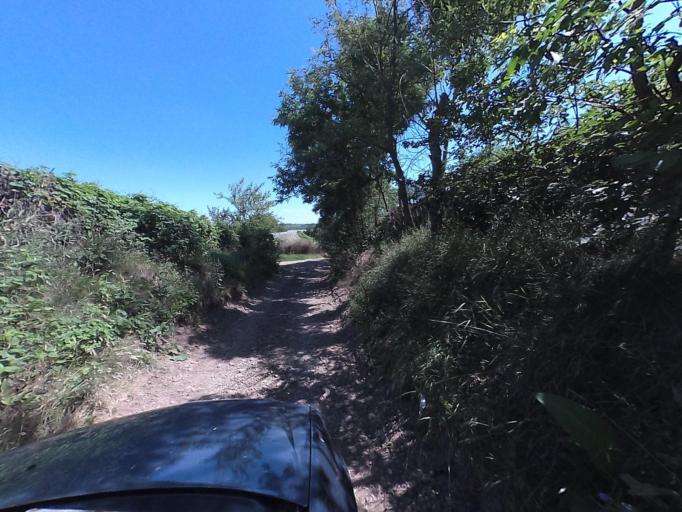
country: RO
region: Vaslui
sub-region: Comuna Costesti
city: Costesti
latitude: 46.4928
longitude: 27.7666
